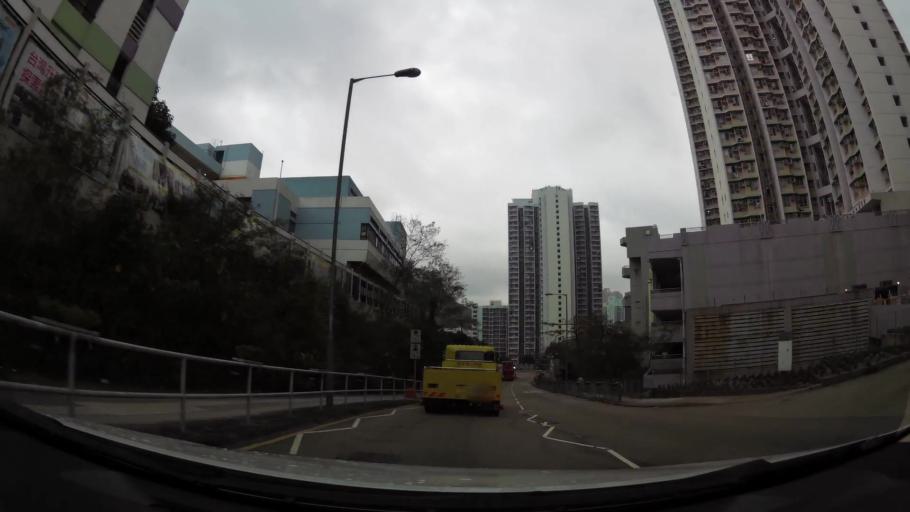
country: HK
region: Tsuen Wan
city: Tsuen Wan
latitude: 22.3655
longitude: 114.1275
